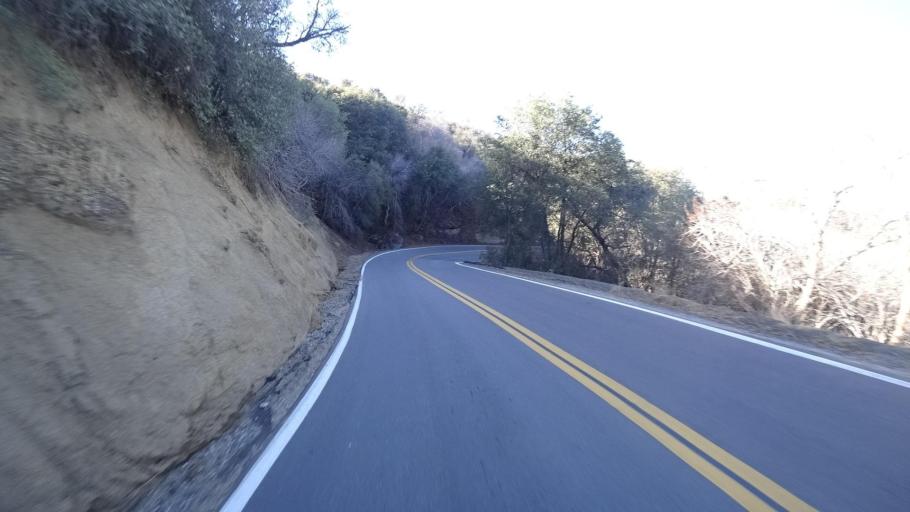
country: US
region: California
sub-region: Kern County
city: Alta Sierra
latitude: 35.7370
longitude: -118.6510
